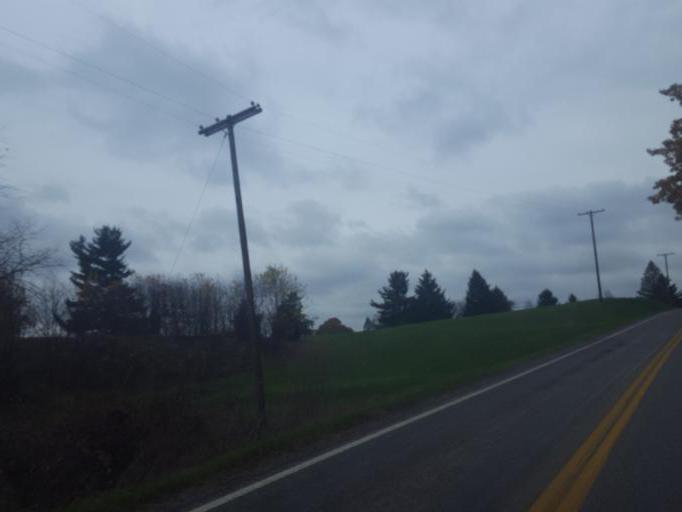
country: US
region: Ohio
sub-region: Ashland County
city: Loudonville
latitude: 40.6710
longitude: -82.1483
